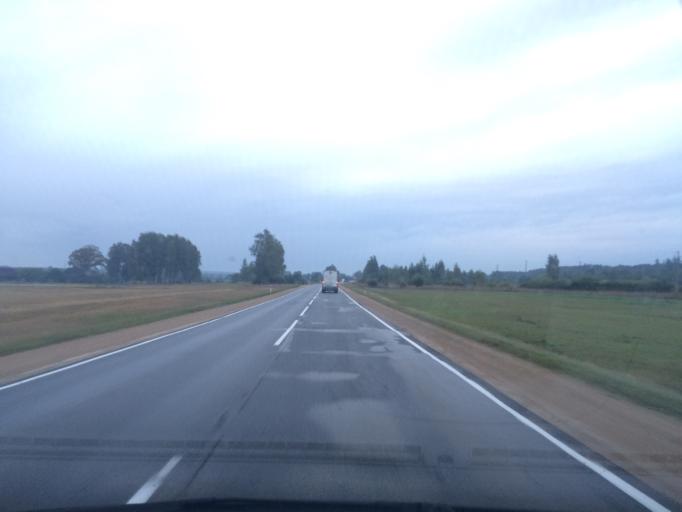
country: LV
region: Plavinu
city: Plavinas
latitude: 56.5827
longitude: 25.7777
